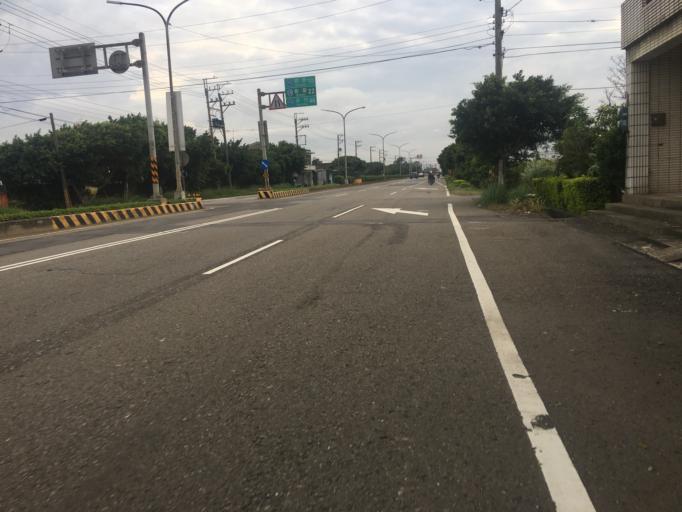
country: TW
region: Taiwan
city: Taoyuan City
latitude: 25.0937
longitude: 121.2328
